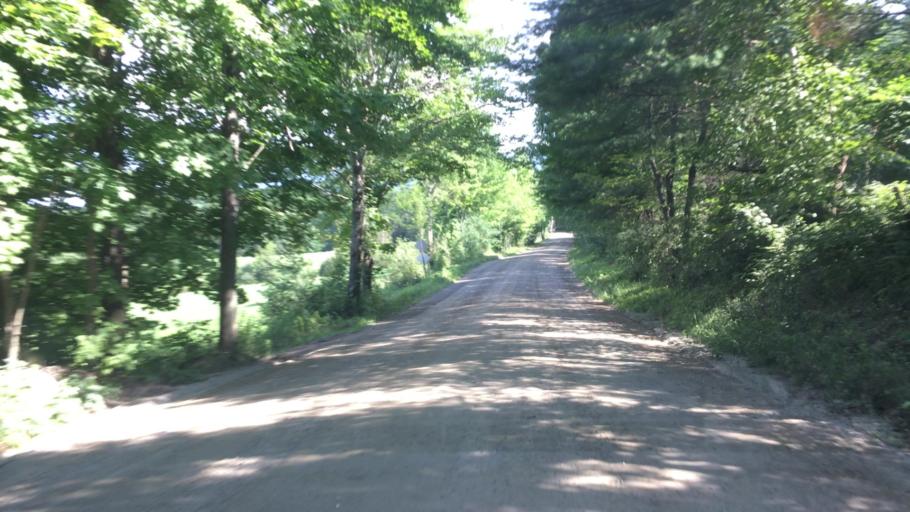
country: US
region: New Hampshire
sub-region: Grafton County
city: Woodsville
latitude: 44.1364
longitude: -71.9702
